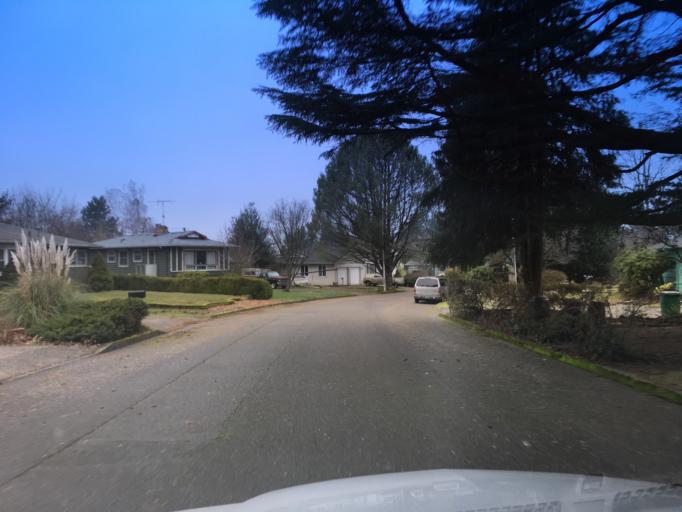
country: US
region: Oregon
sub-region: Multnomah County
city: Fairview
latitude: 45.5415
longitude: -122.5130
